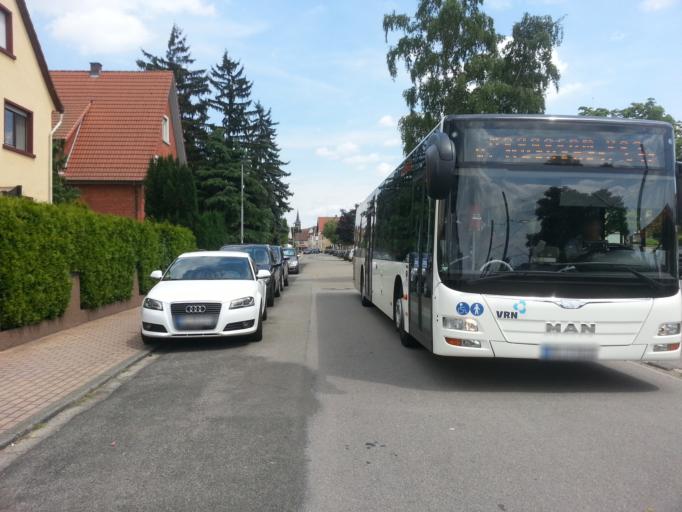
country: DE
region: Baden-Wuerttemberg
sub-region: Karlsruhe Region
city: Heddesheim
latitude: 49.5051
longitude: 8.5955
